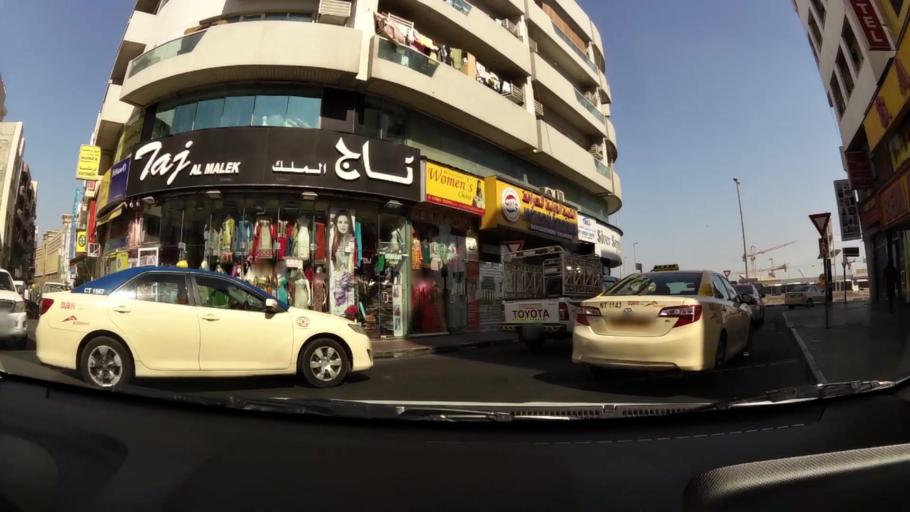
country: AE
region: Ash Shariqah
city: Sharjah
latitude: 25.2747
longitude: 55.3019
